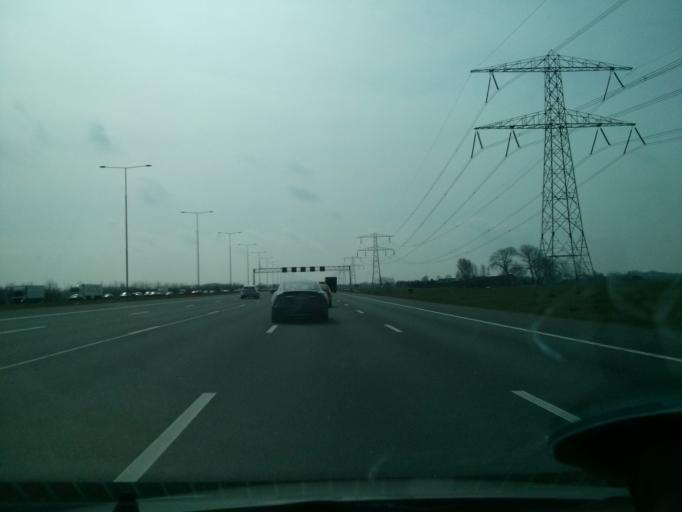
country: NL
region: Utrecht
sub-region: Stichtse Vecht
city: Breukelen
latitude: 52.2035
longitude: 4.9861
